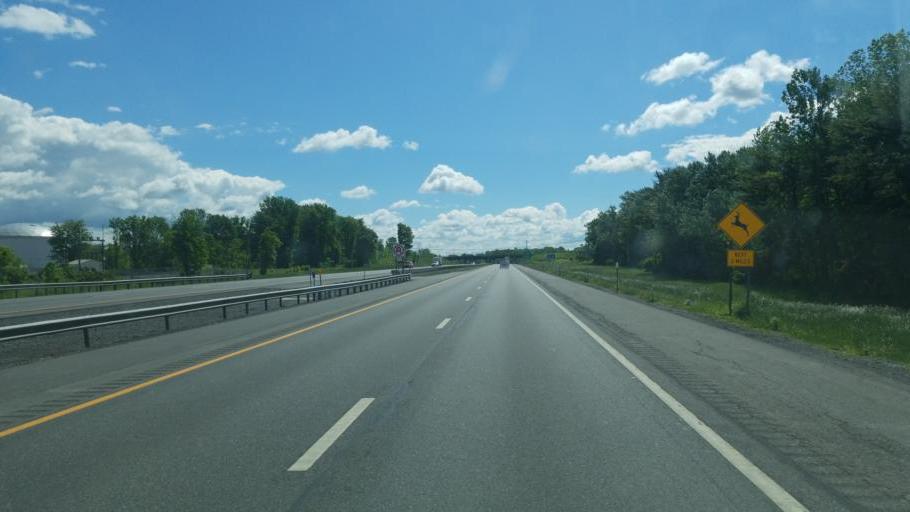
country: US
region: New York
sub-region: Oneida County
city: Sherrill
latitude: 43.1247
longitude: -75.5956
